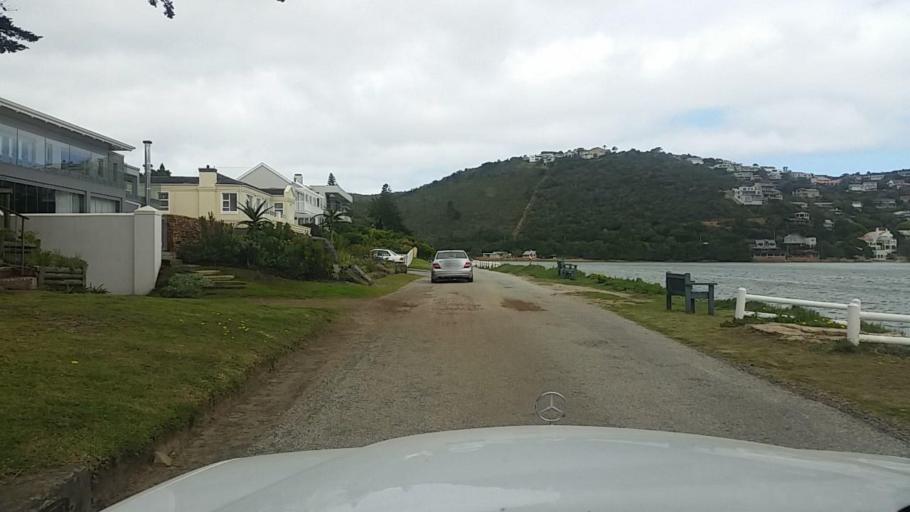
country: ZA
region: Western Cape
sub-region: Eden District Municipality
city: Knysna
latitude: -34.0703
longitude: 23.0604
